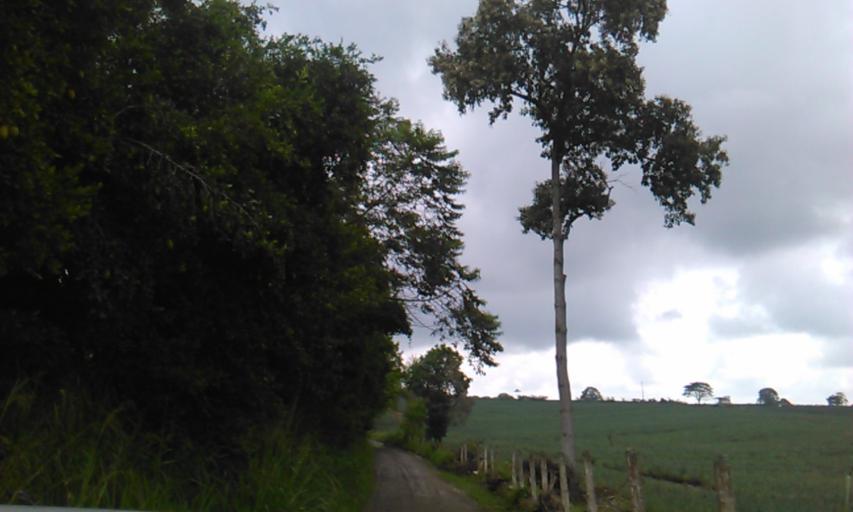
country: CO
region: Quindio
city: La Tebaida
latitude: 4.5070
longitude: -75.8593
